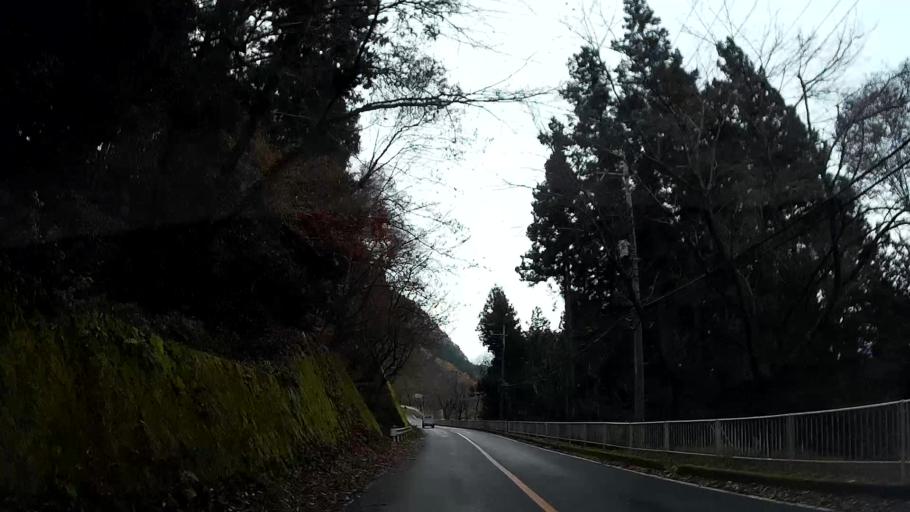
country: JP
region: Saitama
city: Chichibu
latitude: 35.9594
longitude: 139.0561
